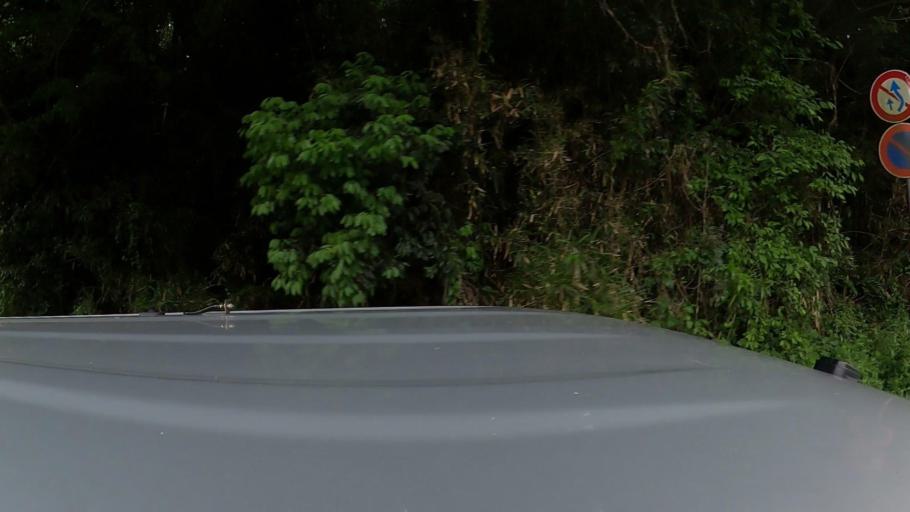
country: JP
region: Ibaraki
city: Ryugasaki
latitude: 35.9552
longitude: 140.2256
